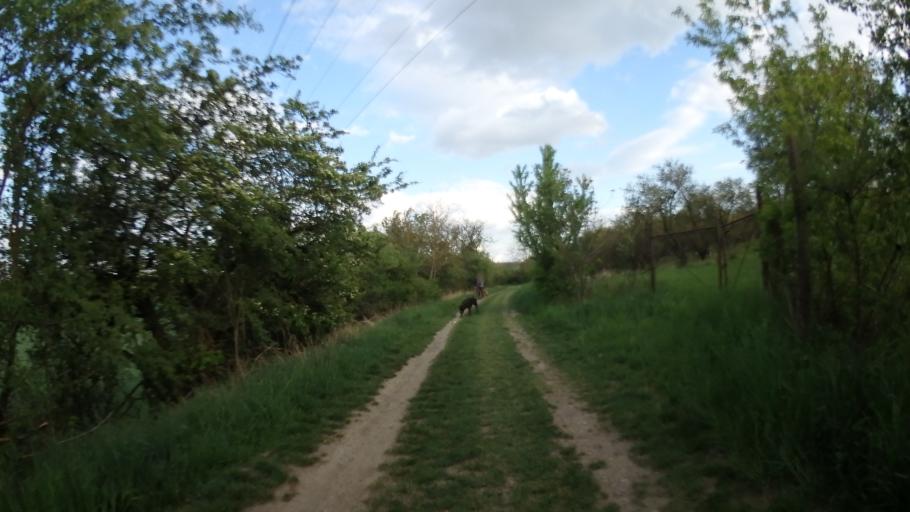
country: CZ
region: South Moravian
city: Moravany
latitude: 49.1592
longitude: 16.5742
